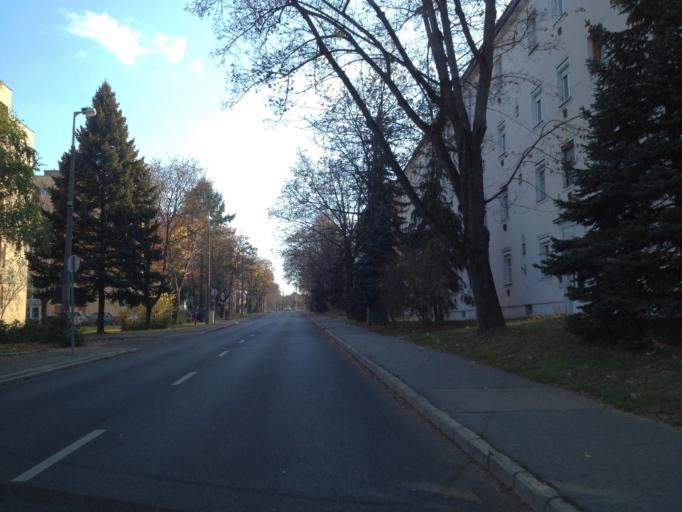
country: HU
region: Veszprem
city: Veszprem
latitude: 47.0846
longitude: 17.9093
